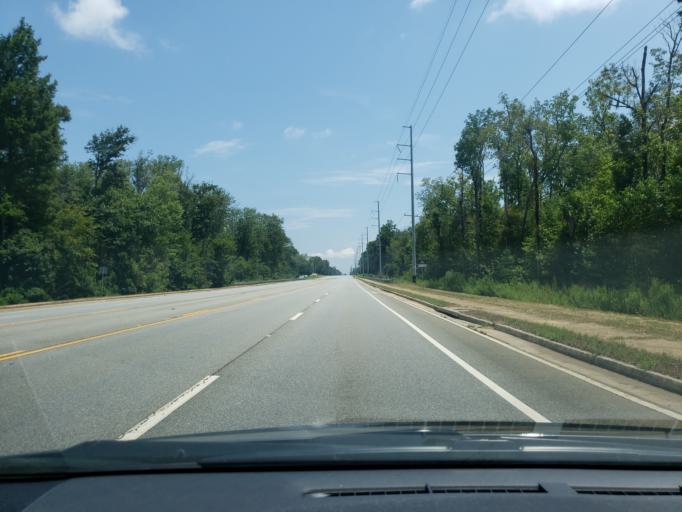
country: US
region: Georgia
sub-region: Dougherty County
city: Albany
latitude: 31.5856
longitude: -84.2666
